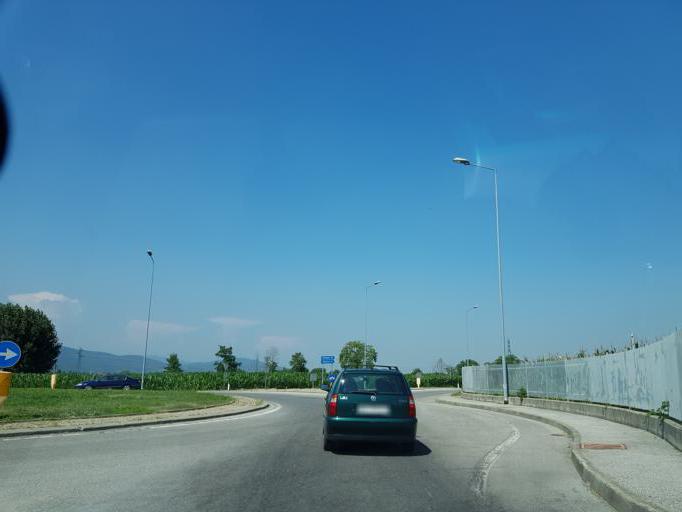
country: IT
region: Piedmont
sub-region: Provincia di Cuneo
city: Caraglio
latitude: 44.4251
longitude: 7.4284
